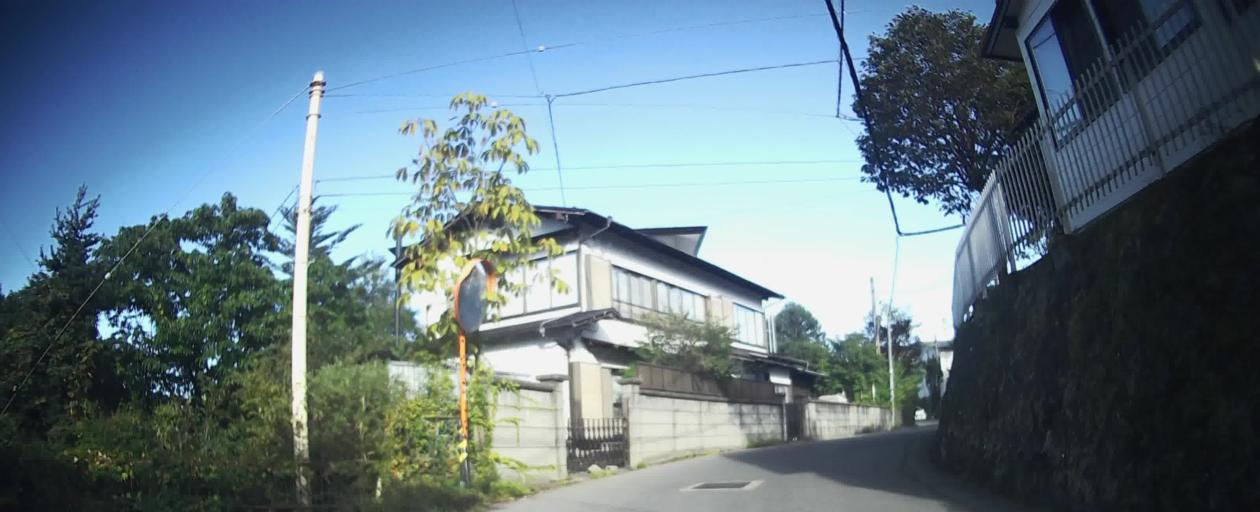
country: JP
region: Gunma
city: Nakanojomachi
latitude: 36.6226
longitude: 138.6022
